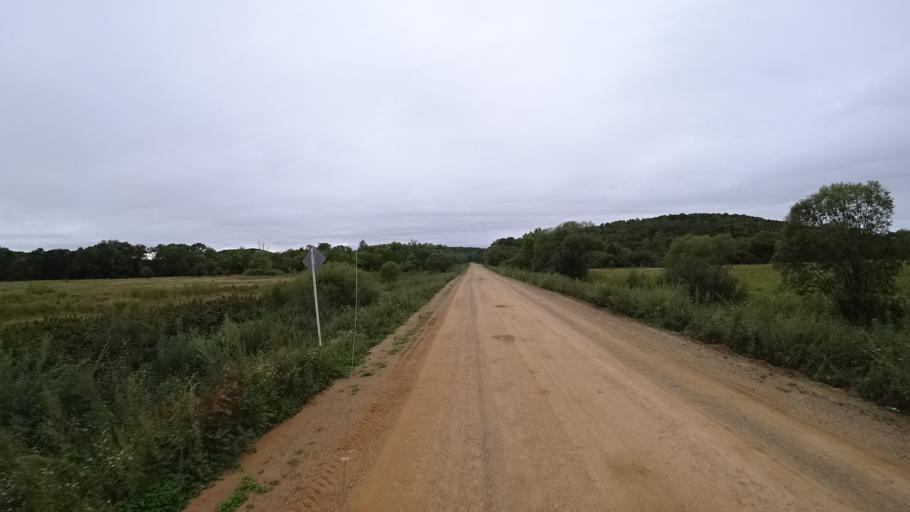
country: RU
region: Primorskiy
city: Rettikhovka
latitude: 44.1746
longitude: 132.8777
